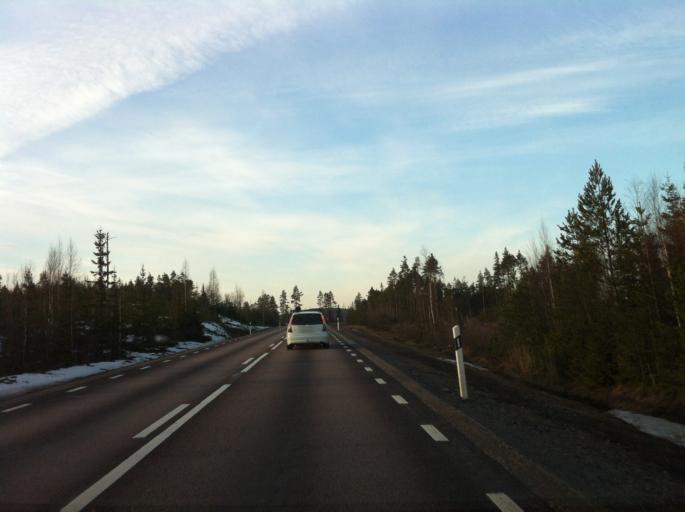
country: SE
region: Vaermland
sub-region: Filipstads Kommun
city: Lesjofors
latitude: 60.0592
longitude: 14.1396
